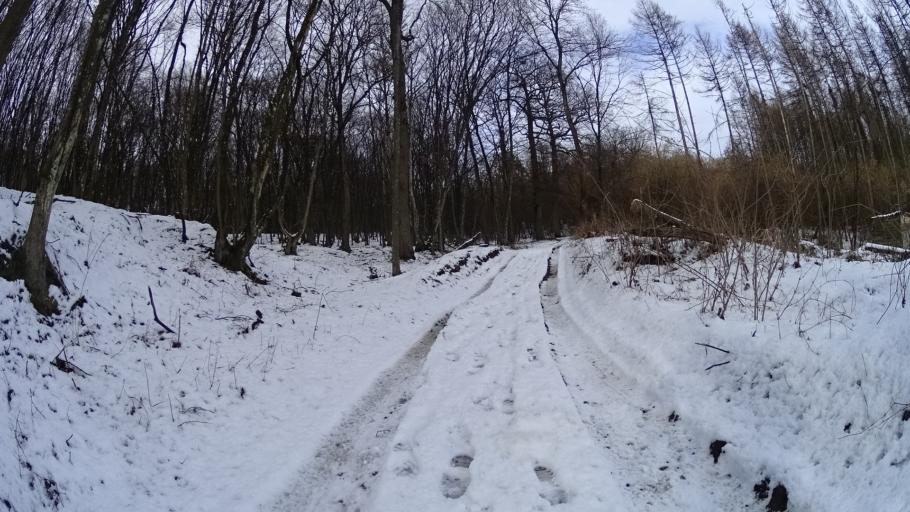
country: AT
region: Lower Austria
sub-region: Politischer Bezirk Korneuburg
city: Niederhollabrunn
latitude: 48.4099
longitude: 16.3036
